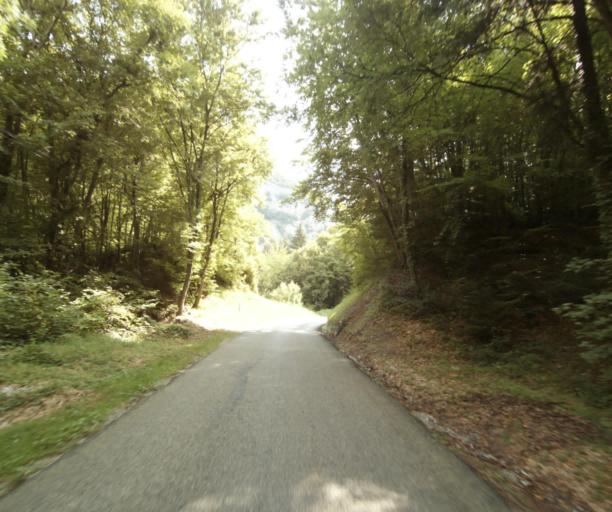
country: FR
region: Rhone-Alpes
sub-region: Departement de l'Isere
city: Le Sappey-en-Chartreuse
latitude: 45.2495
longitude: 5.7393
